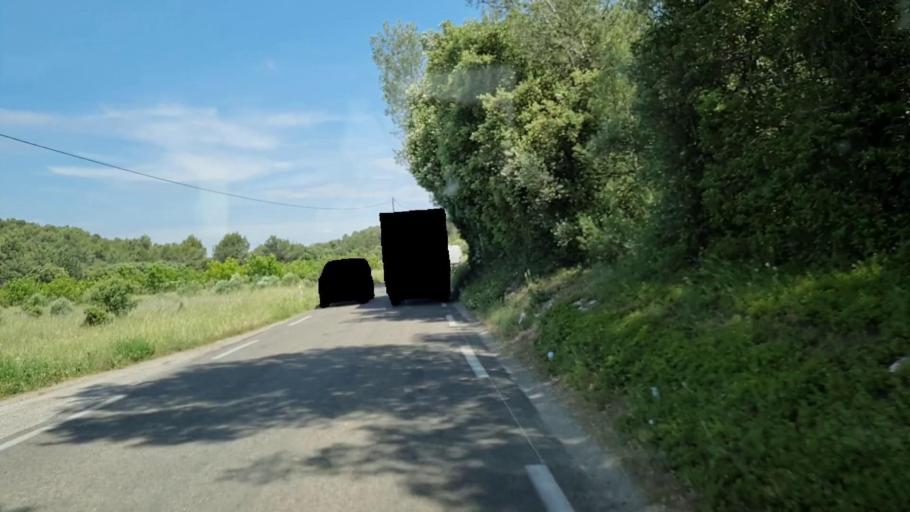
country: FR
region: Languedoc-Roussillon
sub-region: Departement du Gard
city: Saint-Gervasy
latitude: 43.8822
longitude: 4.4682
